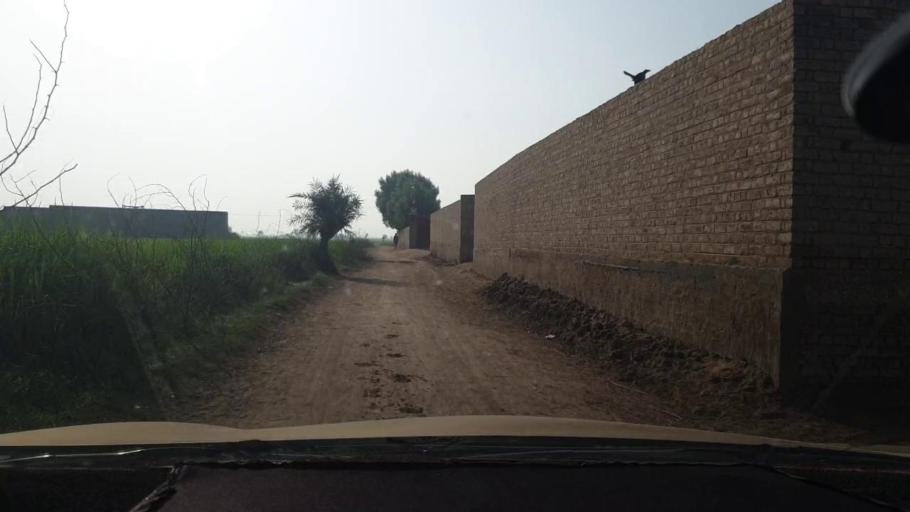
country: PK
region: Sindh
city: Kambar
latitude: 27.5353
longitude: 68.0197
